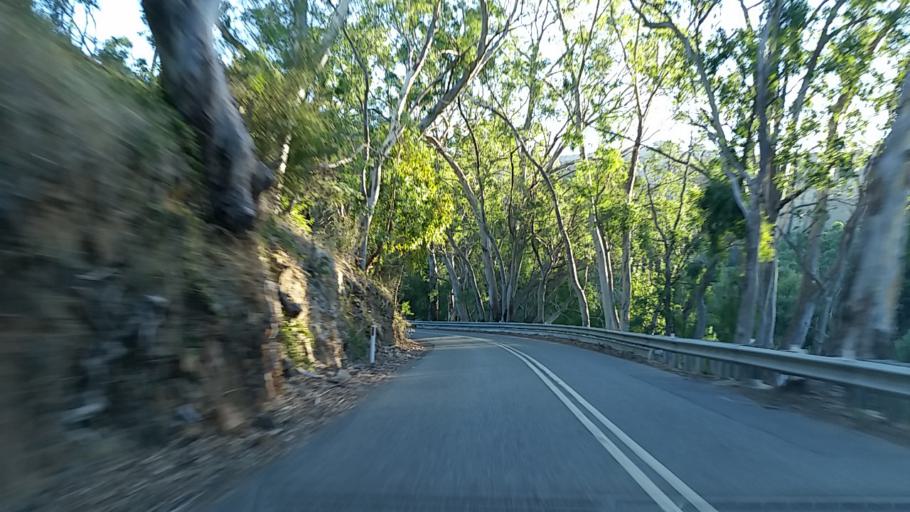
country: AU
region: South Australia
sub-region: Campbelltown
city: Athelstone
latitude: -34.8671
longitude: 138.7570
